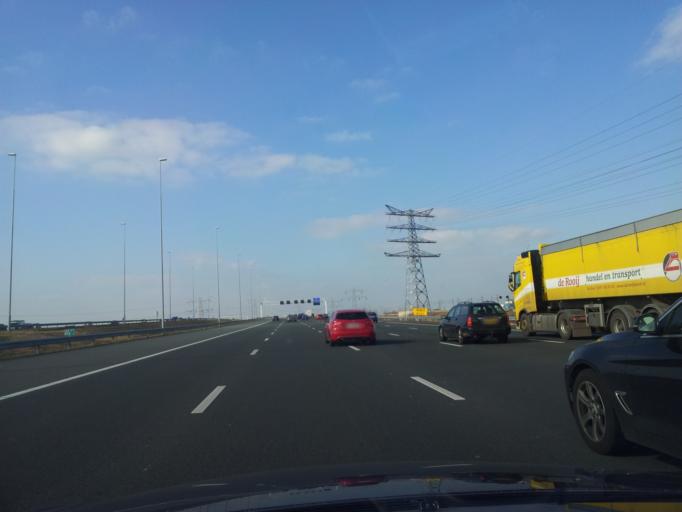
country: NL
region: Utrecht
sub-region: Stichtse Vecht
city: Breukelen
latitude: 52.1566
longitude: 4.9940
